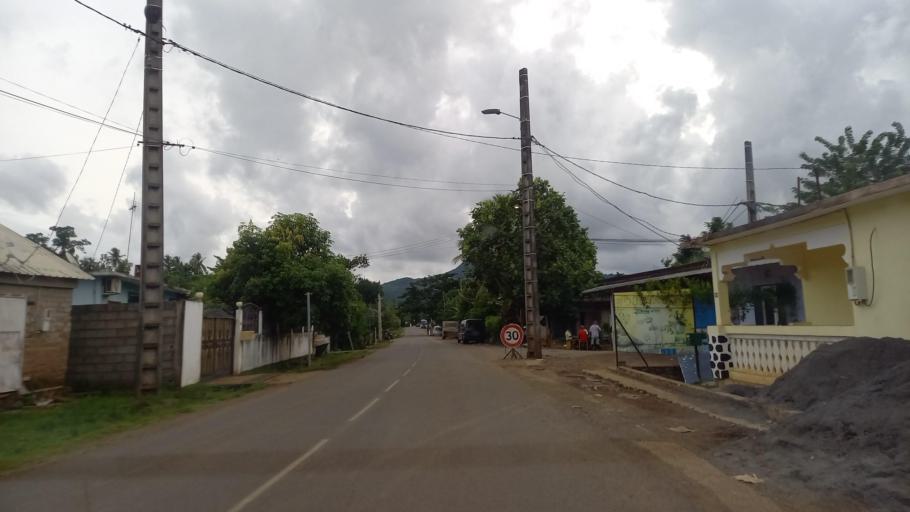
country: YT
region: Chirongui
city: Chirongui
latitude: -12.9204
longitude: 45.1588
